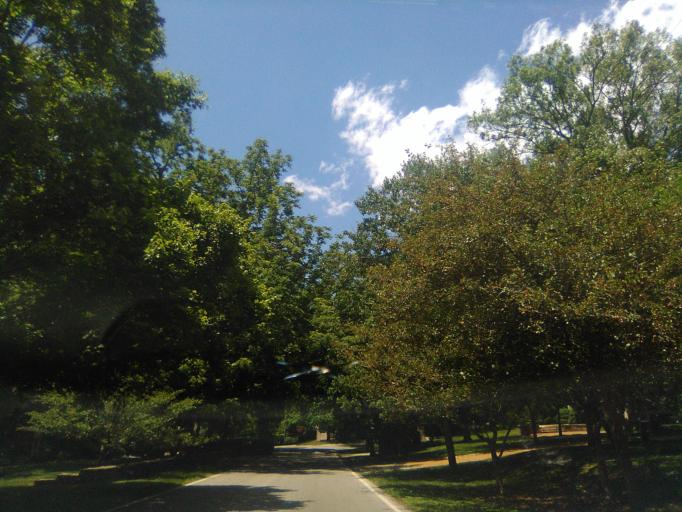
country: US
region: Tennessee
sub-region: Davidson County
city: Belle Meade
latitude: 36.1122
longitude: -86.8570
